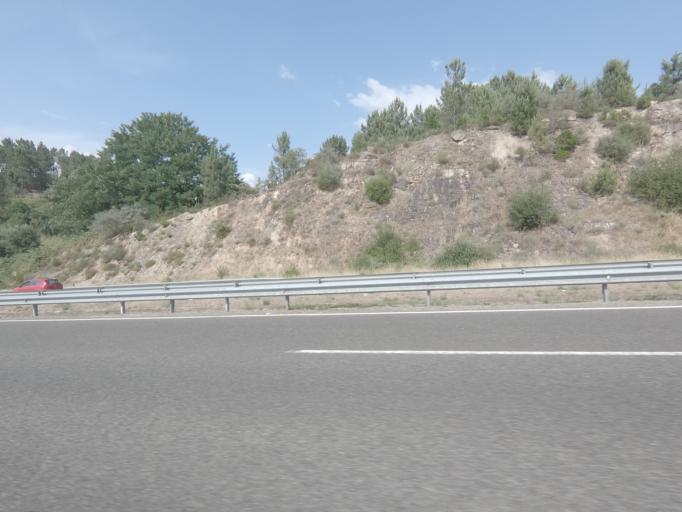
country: ES
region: Galicia
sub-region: Provincia de Ourense
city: Ourense
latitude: 42.2897
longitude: -7.8766
